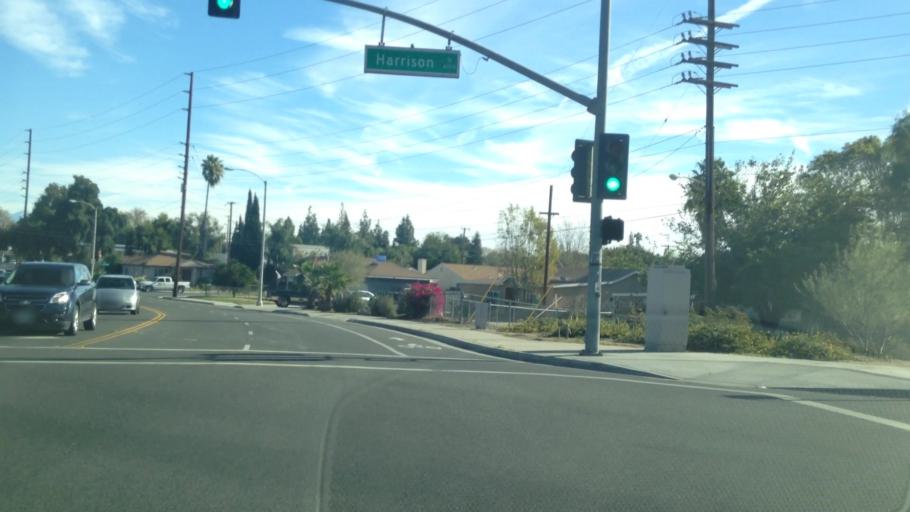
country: US
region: California
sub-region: Riverside County
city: Pedley
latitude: 33.9257
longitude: -117.4539
